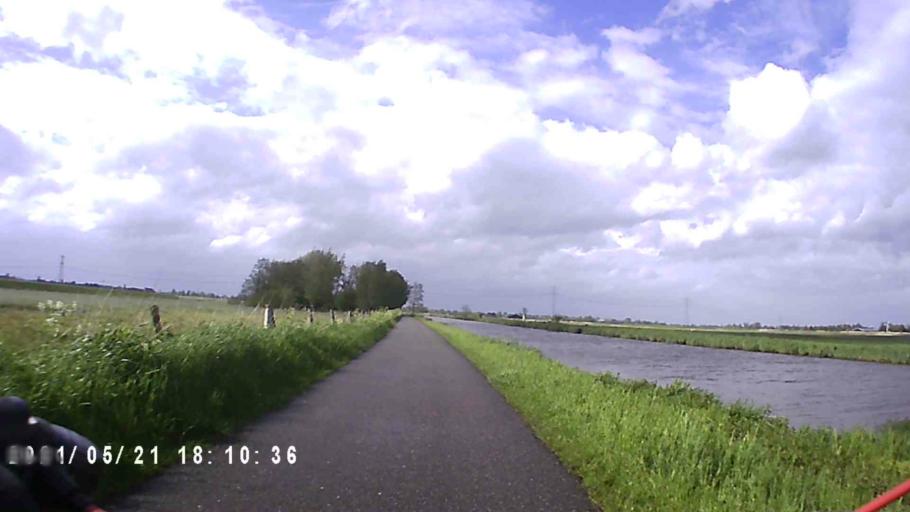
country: NL
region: Groningen
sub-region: Gemeente Zuidhorn
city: Zuidhorn
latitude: 53.2035
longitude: 6.4128
